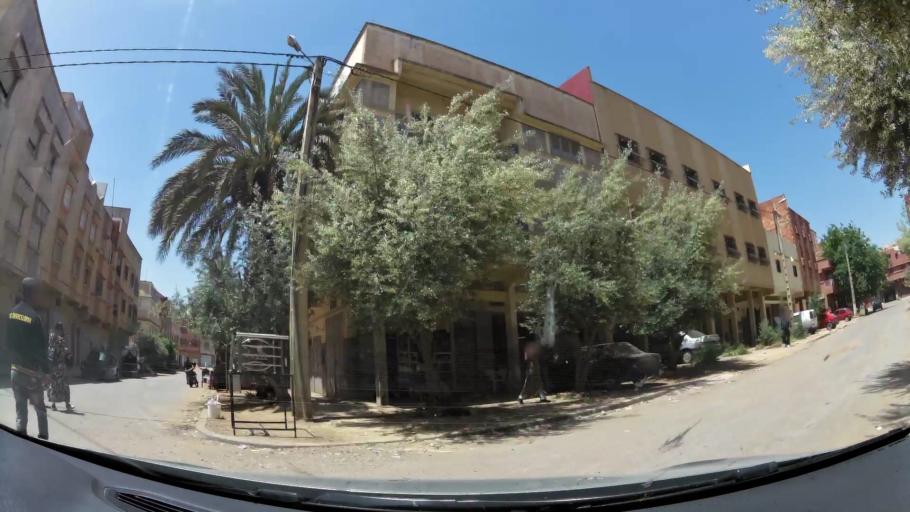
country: MA
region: Rabat-Sale-Zemmour-Zaer
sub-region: Khemisset
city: Khemisset
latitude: 33.8316
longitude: -6.0692
